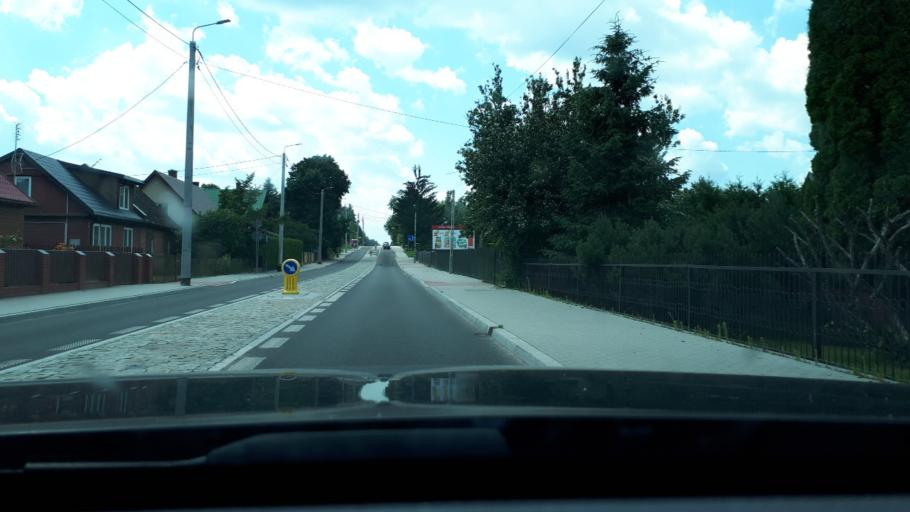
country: PL
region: Podlasie
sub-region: Powiat bialostocki
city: Suprasl
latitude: 53.2076
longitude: 23.3251
